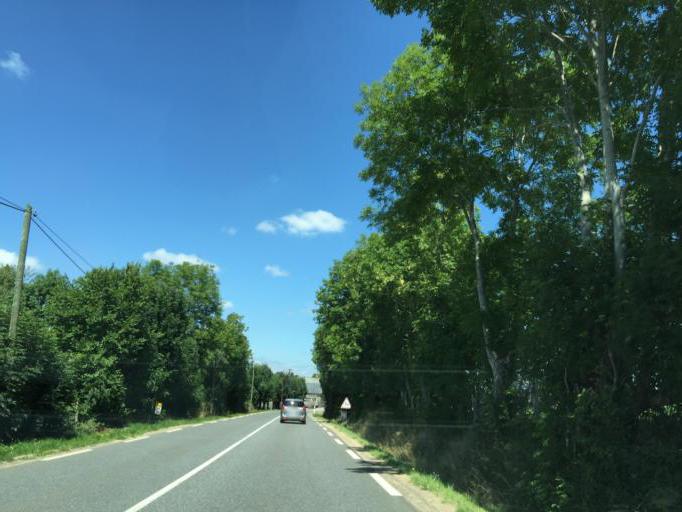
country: FR
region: Midi-Pyrenees
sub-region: Departement de l'Aveyron
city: Laguiole
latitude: 44.6096
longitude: 2.8058
